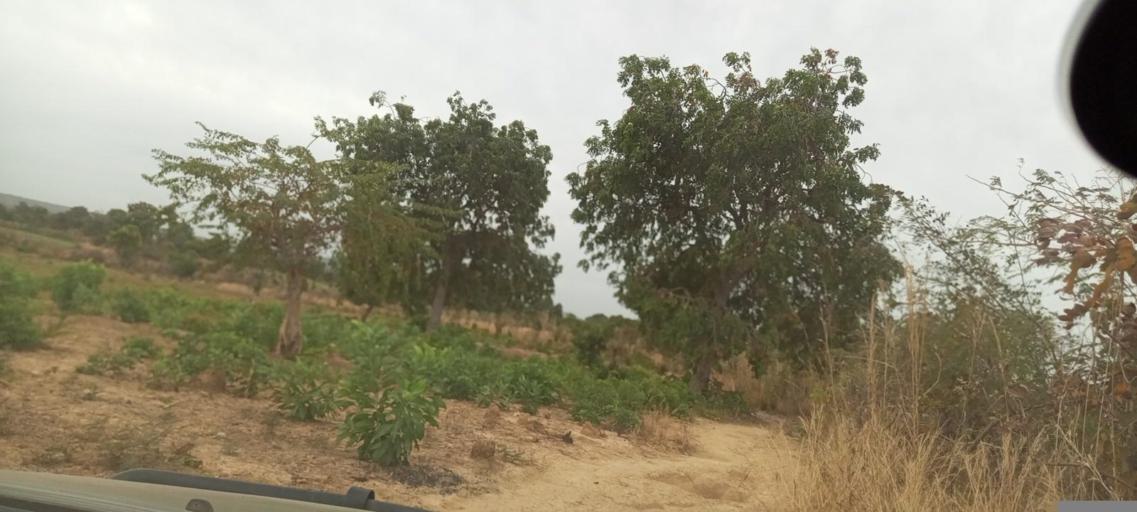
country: ML
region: Koulikoro
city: Kati
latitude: 12.7453
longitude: -8.3533
